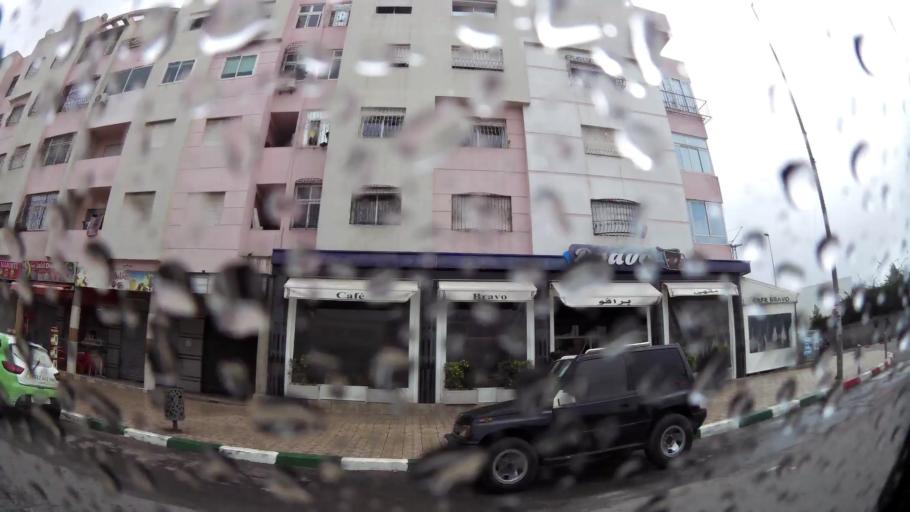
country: MA
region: Grand Casablanca
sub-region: Mediouna
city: Tit Mellil
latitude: 33.6144
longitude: -7.4887
